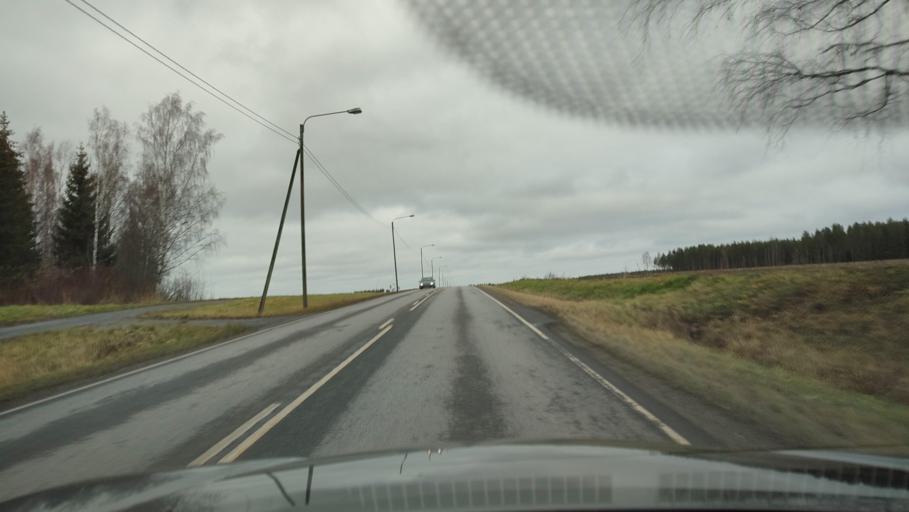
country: FI
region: Southern Ostrobothnia
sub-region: Seinaejoki
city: Kurikka
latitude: 62.5945
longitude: 22.4130
